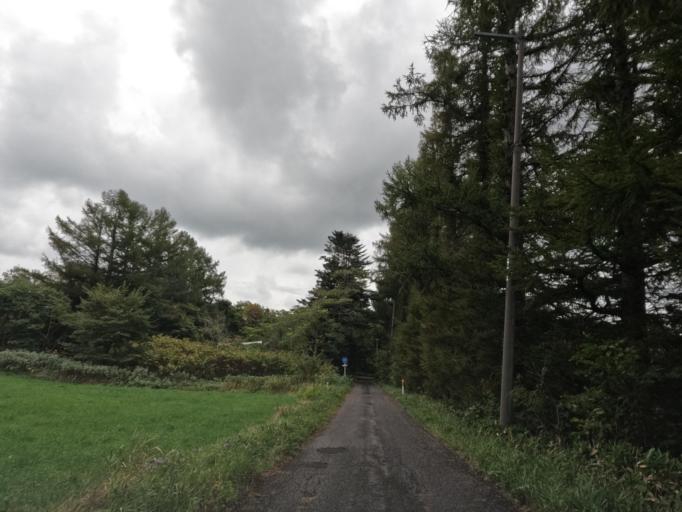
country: JP
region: Hokkaido
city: Date
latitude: 42.4869
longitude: 140.9043
